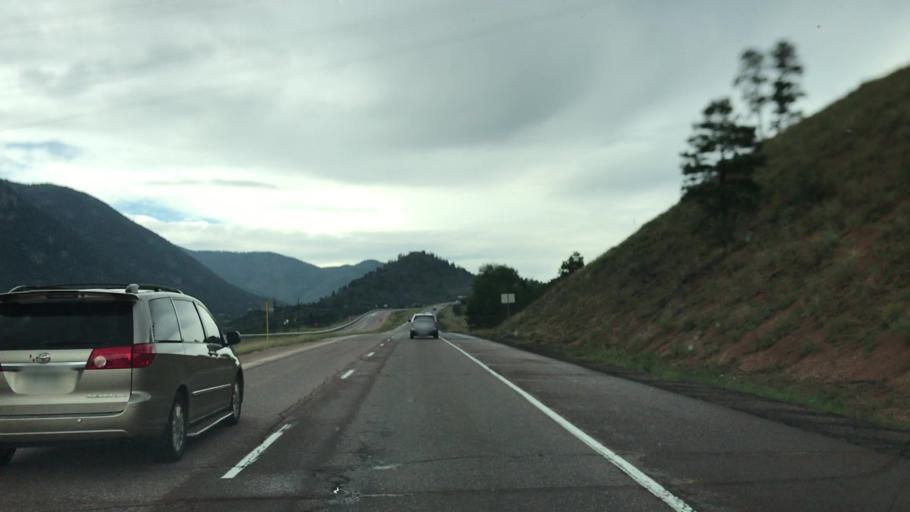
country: US
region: Colorado
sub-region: El Paso County
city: Cascade-Chipita Park
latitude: 38.9217
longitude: -104.9900
